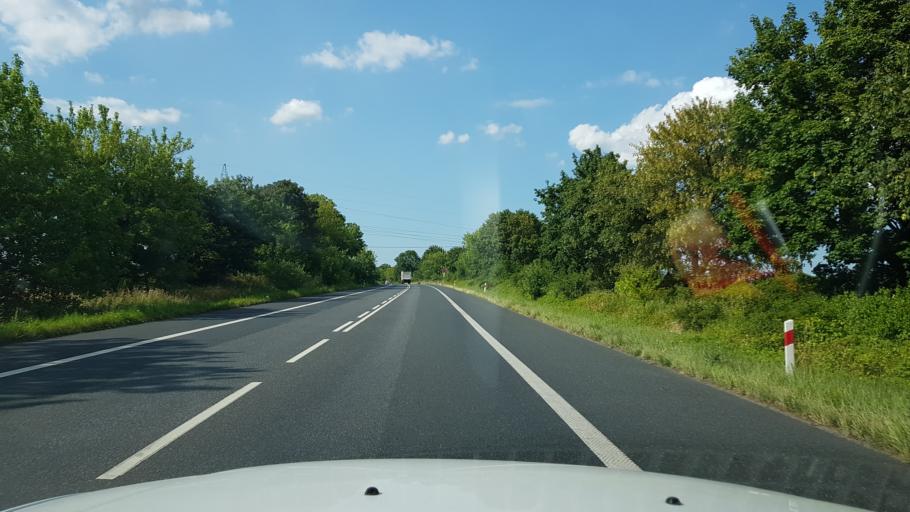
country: PL
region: West Pomeranian Voivodeship
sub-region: Powiat gryfinski
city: Stare Czarnowo
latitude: 53.2628
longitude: 14.7842
